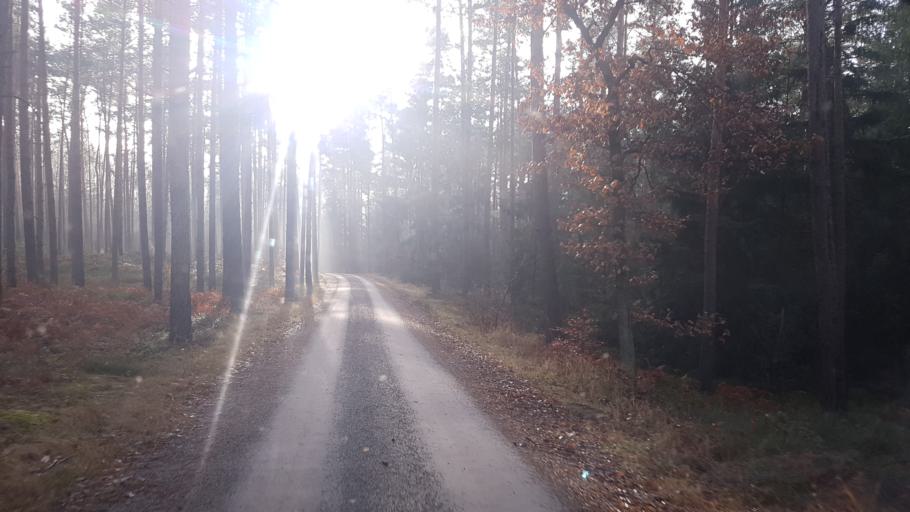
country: DE
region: Brandenburg
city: Schonborn
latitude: 51.6249
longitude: 13.5087
